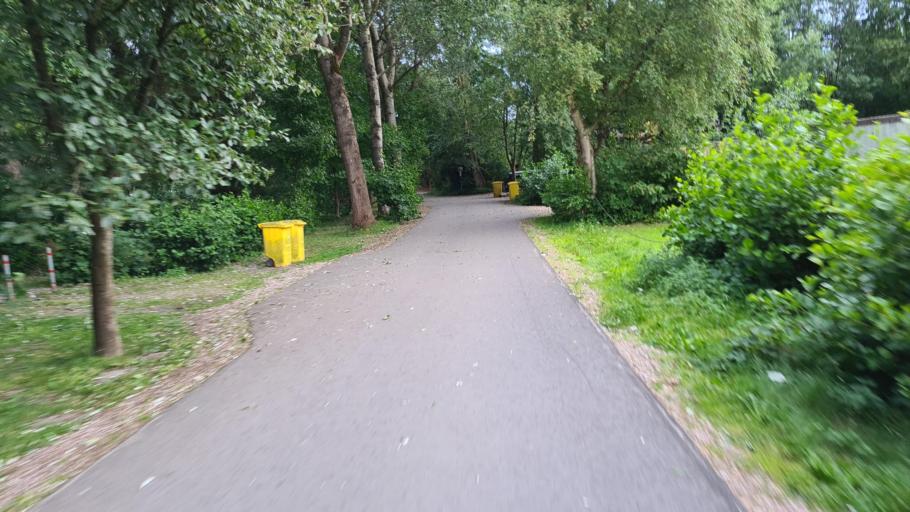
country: DE
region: Schleswig-Holstein
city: Sankt Peter-Ording
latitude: 54.2917
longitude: 8.6501
